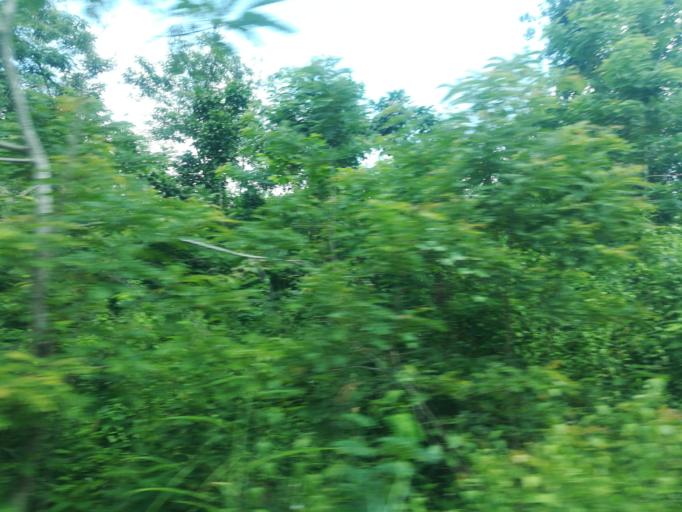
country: NG
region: Oyo
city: Moniya
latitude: 7.5840
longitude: 3.9142
